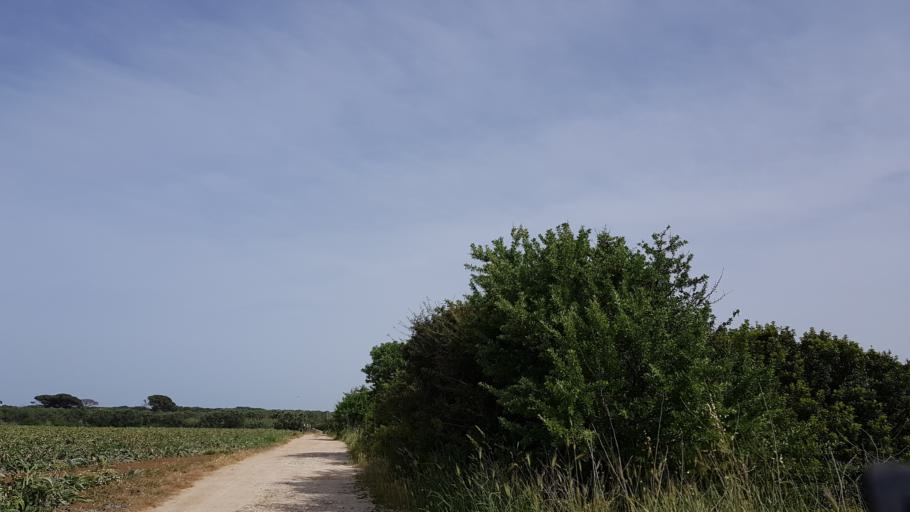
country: IT
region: Apulia
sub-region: Provincia di Brindisi
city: La Rosa
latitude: 40.5917
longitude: 17.9983
